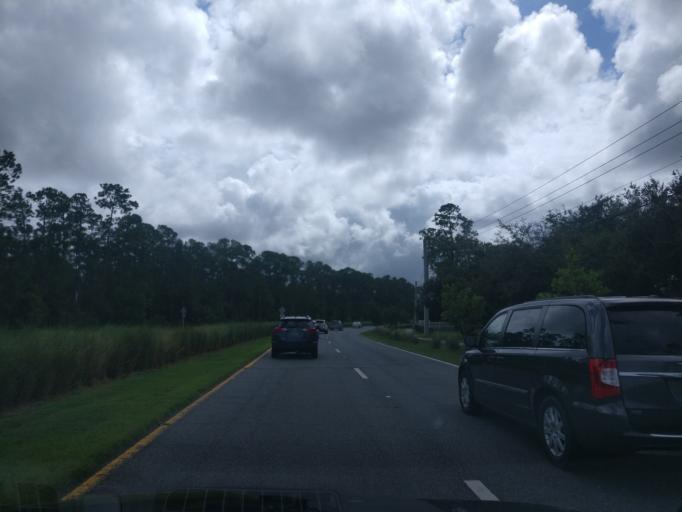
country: US
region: Florida
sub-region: Flagler County
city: Bunnell
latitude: 29.4942
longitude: -81.2198
